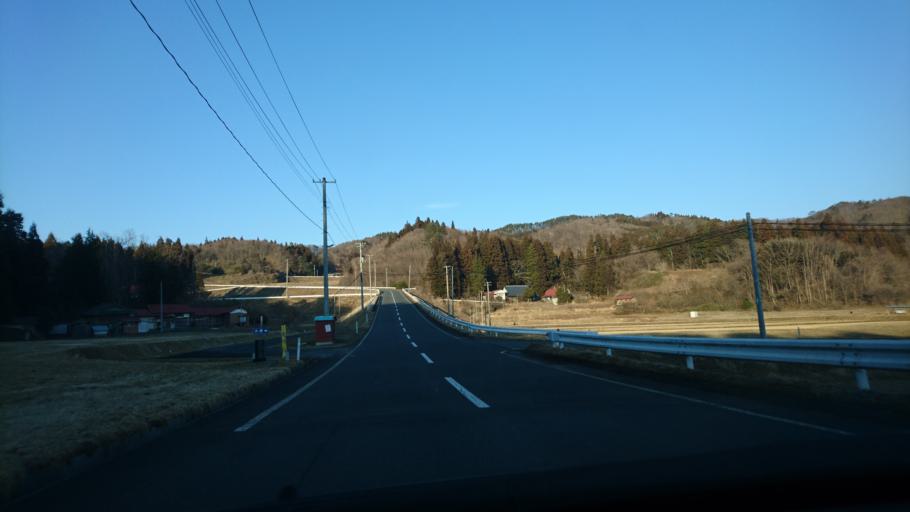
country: JP
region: Iwate
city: Ichinoseki
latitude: 39.0231
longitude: 141.3734
